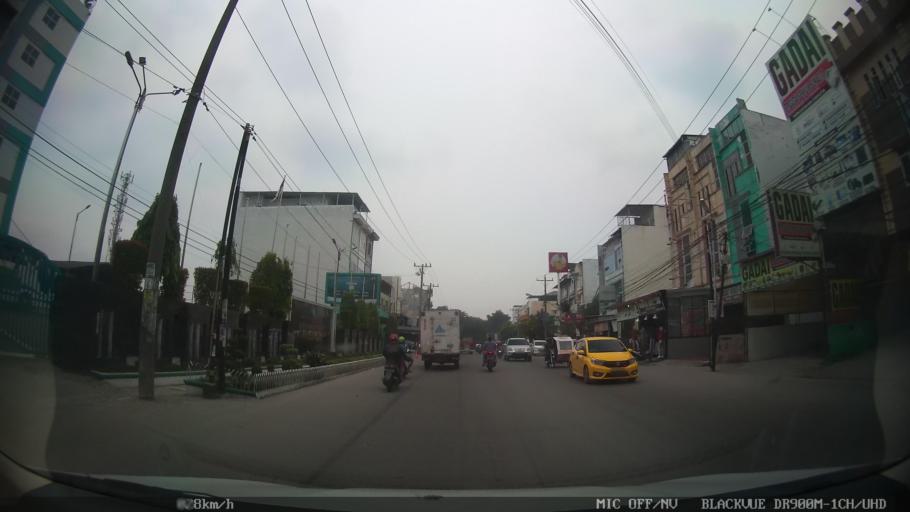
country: ID
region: North Sumatra
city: Medan
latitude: 3.5815
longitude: 98.7212
